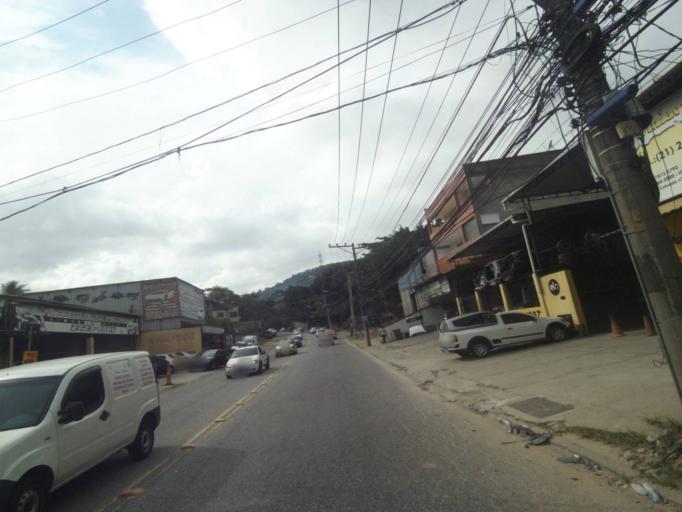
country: BR
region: Rio de Janeiro
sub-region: Sao Joao De Meriti
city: Sao Joao de Meriti
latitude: -22.9092
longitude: -43.3785
